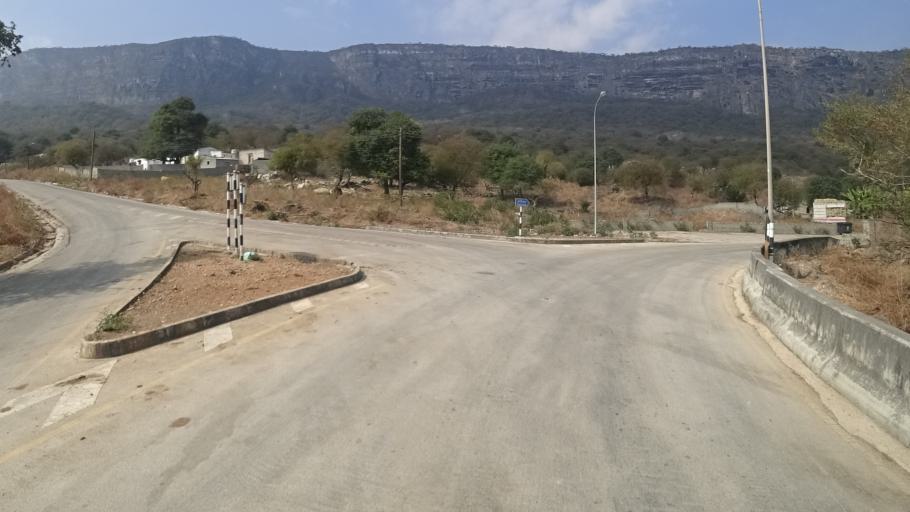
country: YE
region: Al Mahrah
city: Hawf
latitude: 16.7132
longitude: 53.2515
